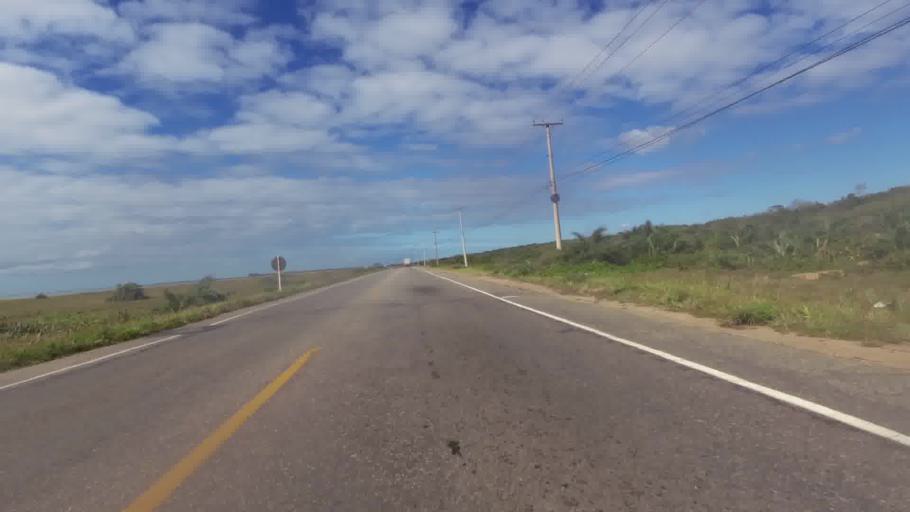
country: BR
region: Espirito Santo
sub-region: Itapemirim
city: Itapemirim
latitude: -20.9697
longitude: -40.8110
